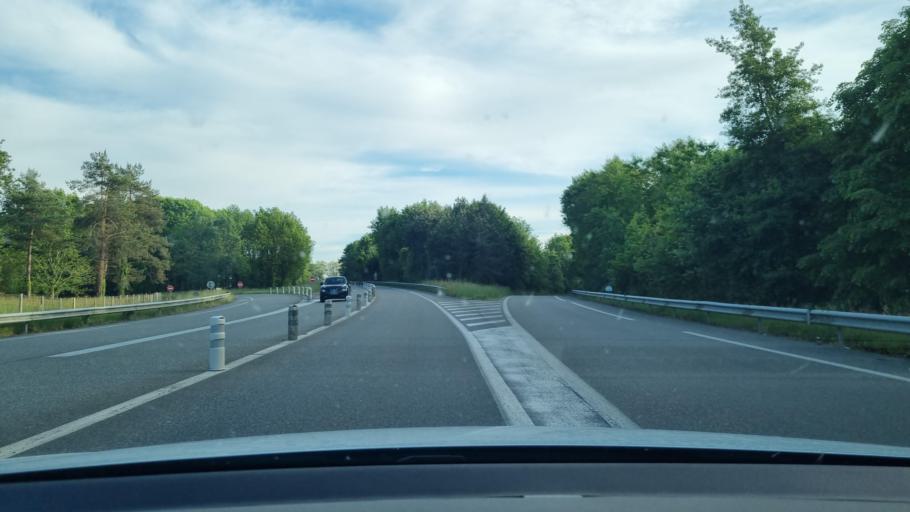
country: FR
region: Aquitaine
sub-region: Departement des Landes
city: Peyrehorade
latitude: 43.5161
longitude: -1.1042
